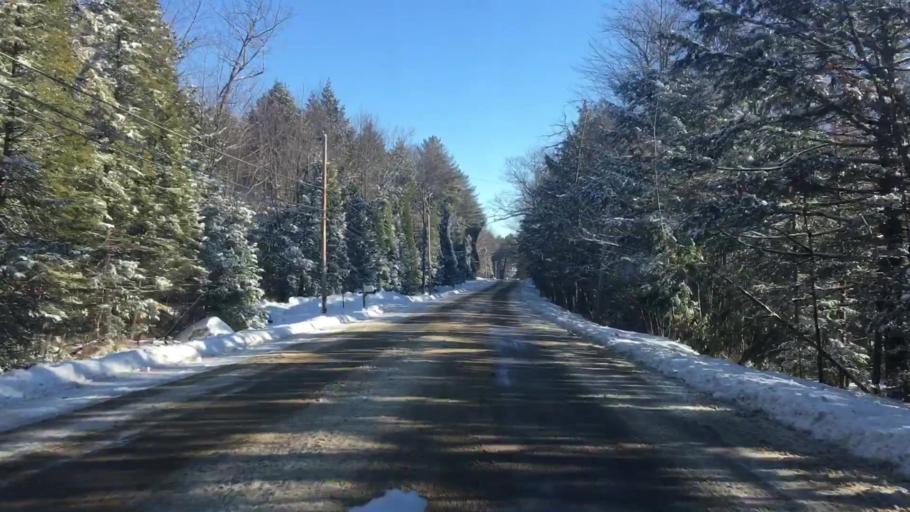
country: US
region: Maine
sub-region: Cumberland County
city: New Gloucester
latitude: 43.9528
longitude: -70.3107
